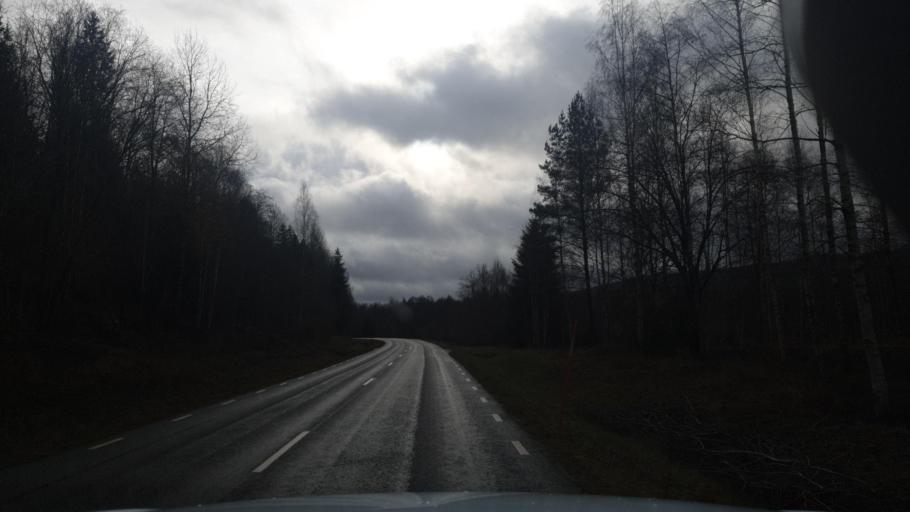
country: SE
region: Vaermland
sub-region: Eda Kommun
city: Amotfors
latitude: 59.6932
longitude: 12.0916
